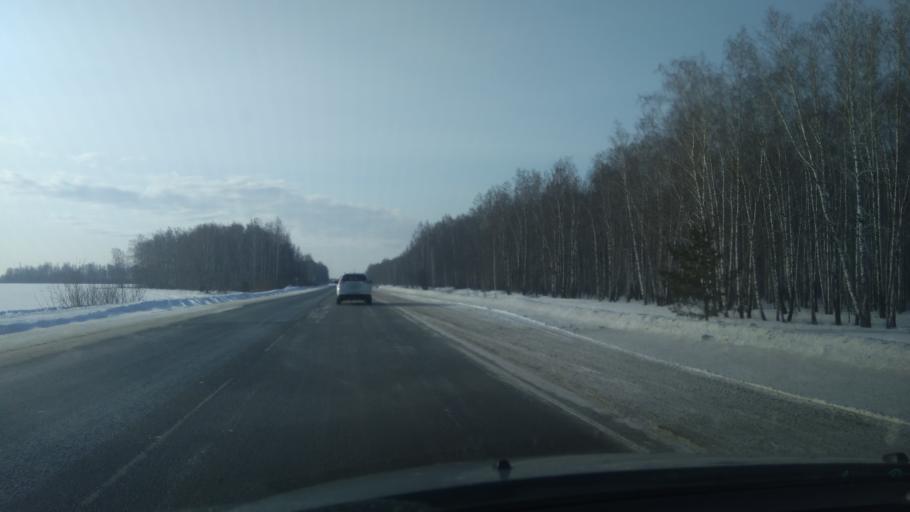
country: RU
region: Sverdlovsk
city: Bogdanovich
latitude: 56.8072
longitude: 62.0326
